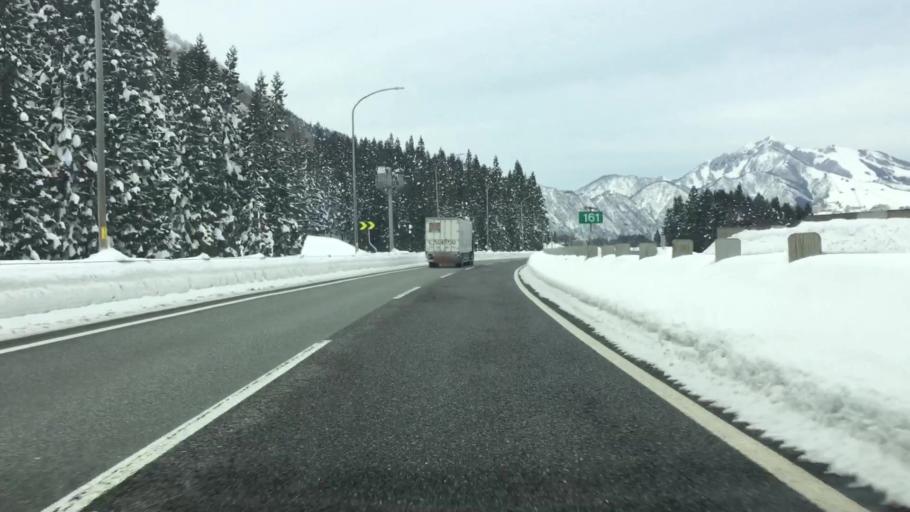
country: JP
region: Niigata
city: Shiozawa
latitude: 36.8874
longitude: 138.8491
